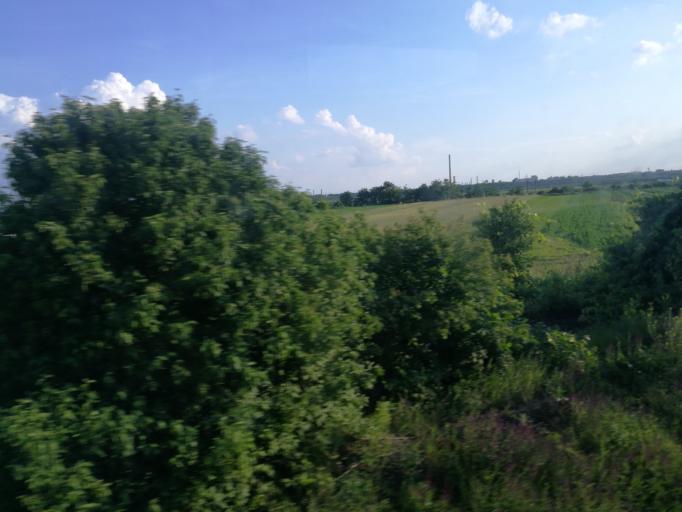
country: RO
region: Arges
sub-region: Oras Stefanesti
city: Golesti
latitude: 44.8381
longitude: 24.9532
